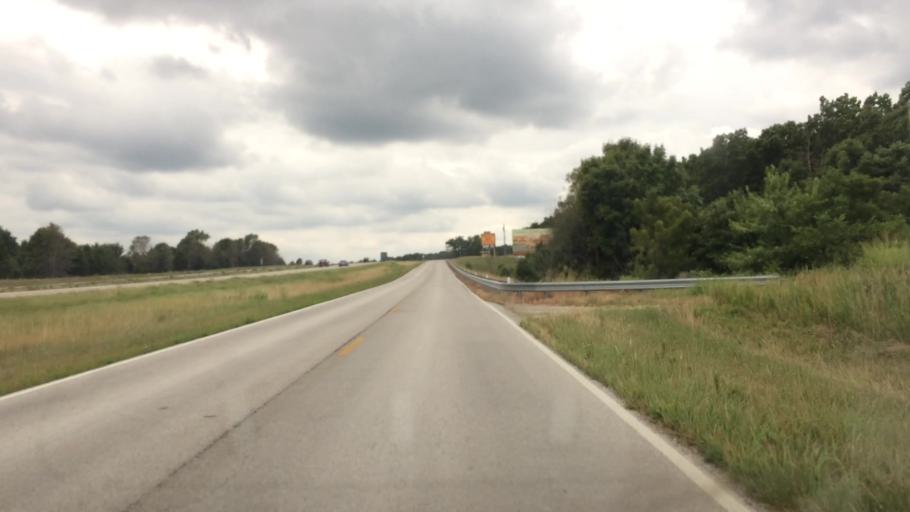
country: US
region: Missouri
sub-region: Greene County
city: Strafford
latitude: 37.2871
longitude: -93.0362
